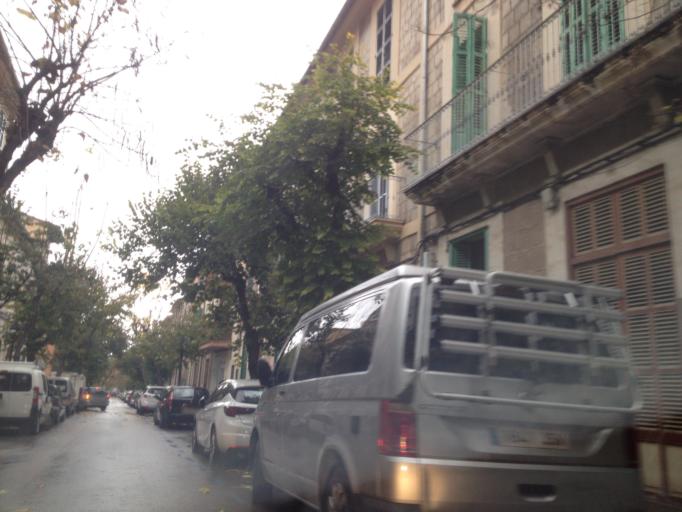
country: ES
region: Balearic Islands
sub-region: Illes Balears
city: Soller
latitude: 39.7689
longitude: 2.7117
